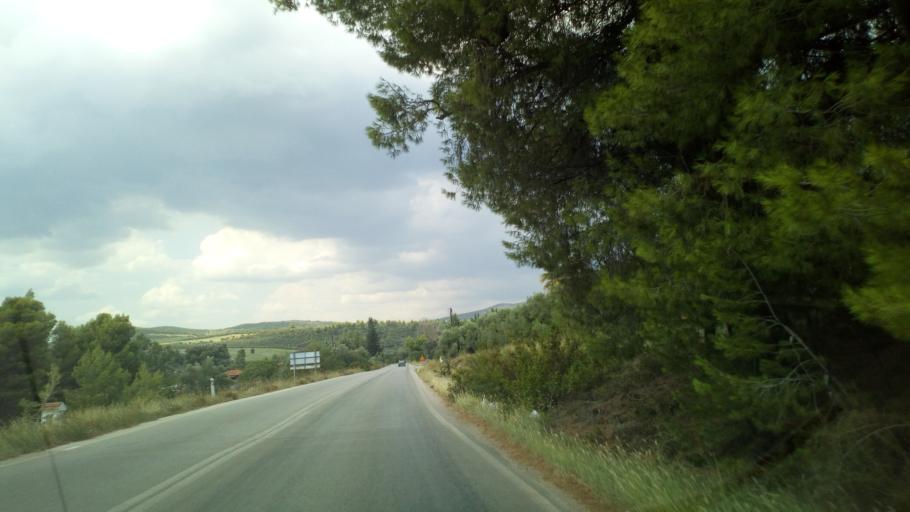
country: GR
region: Central Macedonia
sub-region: Nomos Chalkidikis
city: Nikiti
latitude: 40.2340
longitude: 23.6009
